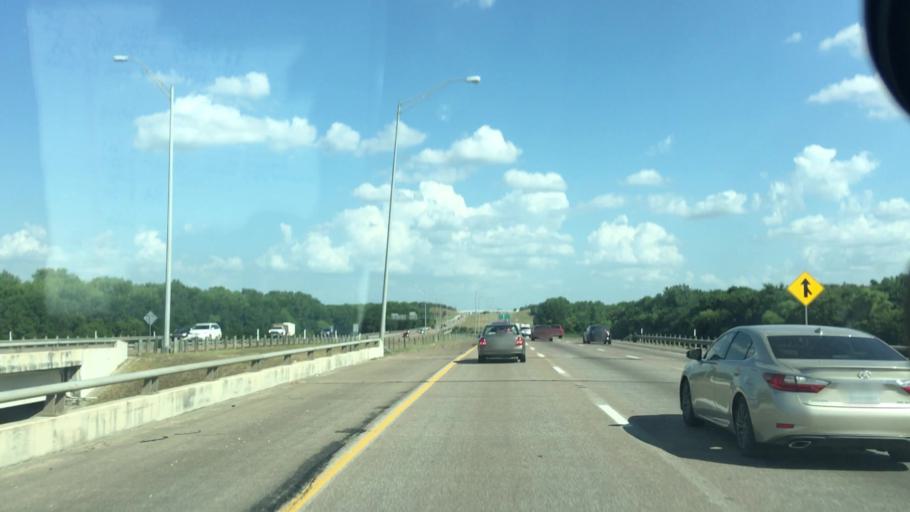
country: US
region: Texas
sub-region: Dallas County
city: Hutchins
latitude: 32.6817
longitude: -96.7445
